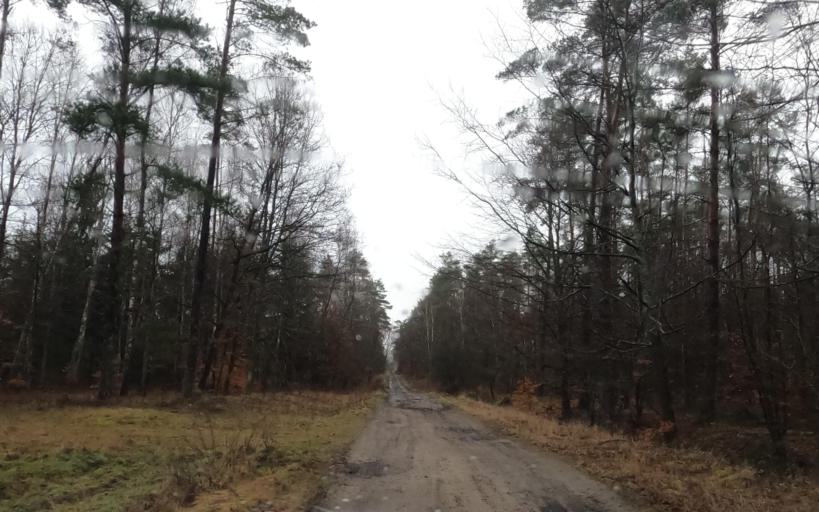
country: PL
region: West Pomeranian Voivodeship
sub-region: Powiat szczecinecki
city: Szczecinek
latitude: 53.6089
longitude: 16.6677
